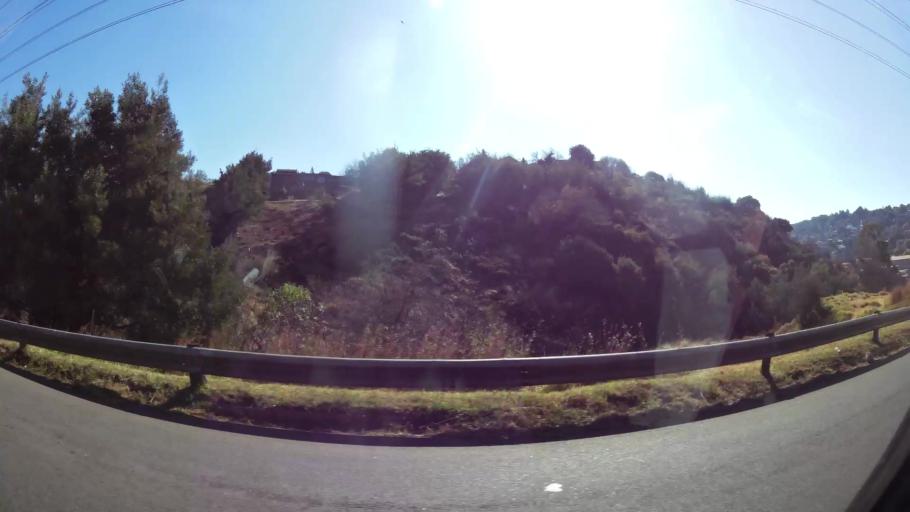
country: ZA
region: Gauteng
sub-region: City of Johannesburg Metropolitan Municipality
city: Roodepoort
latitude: -26.1248
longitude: 27.8716
